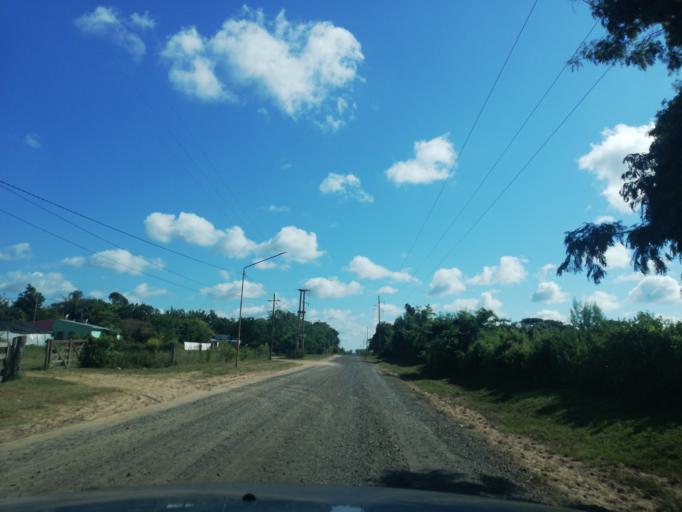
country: AR
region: Corrientes
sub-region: Departamento de San Miguel
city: San Miguel
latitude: -27.9881
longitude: -57.5860
